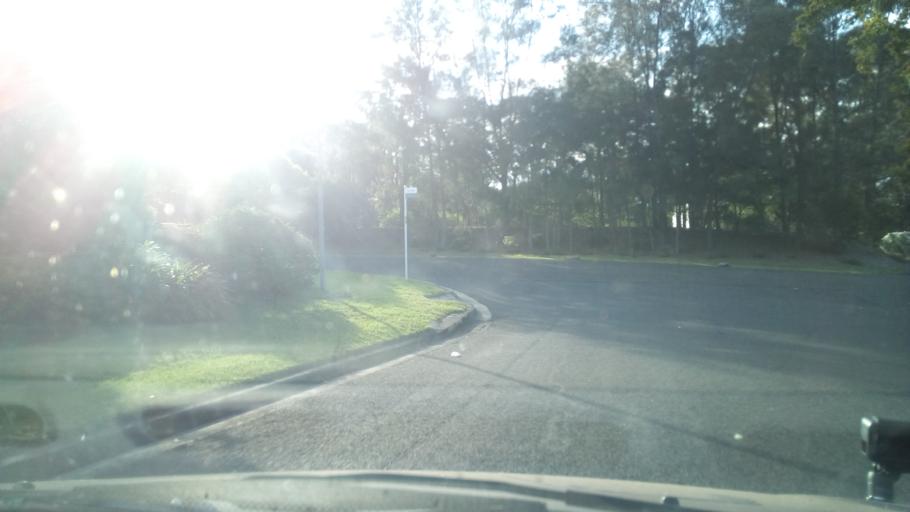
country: AU
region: New South Wales
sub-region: Wollongong
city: Mount Ousley
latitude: -34.3840
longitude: 150.8716
